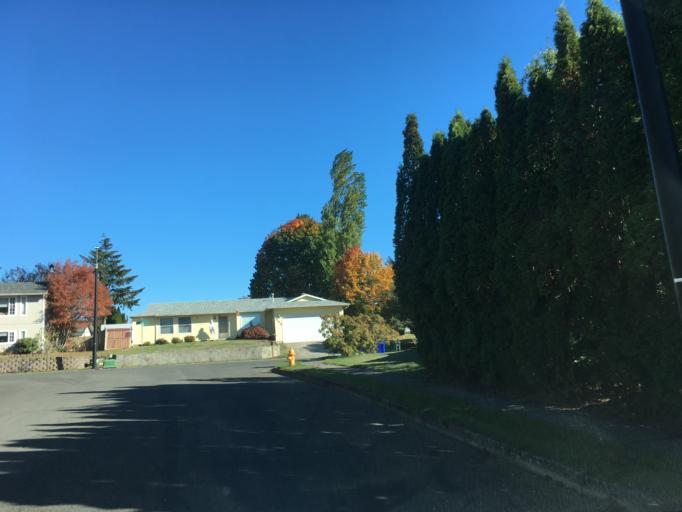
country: US
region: Oregon
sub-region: Multnomah County
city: Gresham
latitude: 45.4954
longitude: -122.4013
